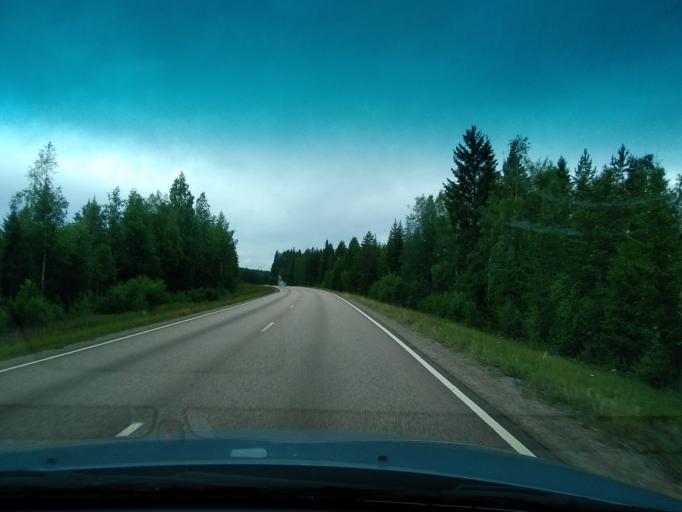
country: FI
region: Central Finland
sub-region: Keuruu
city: Multia
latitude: 62.3854
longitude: 24.7557
